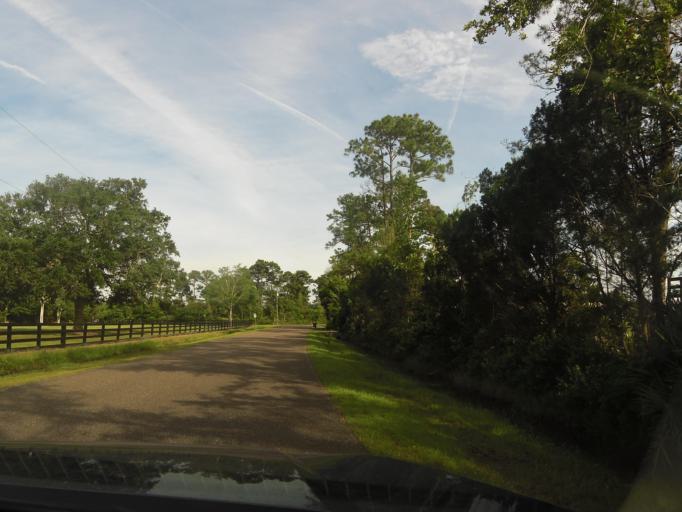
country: US
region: Florida
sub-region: Nassau County
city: Fernandina Beach
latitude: 30.5162
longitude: -81.4865
